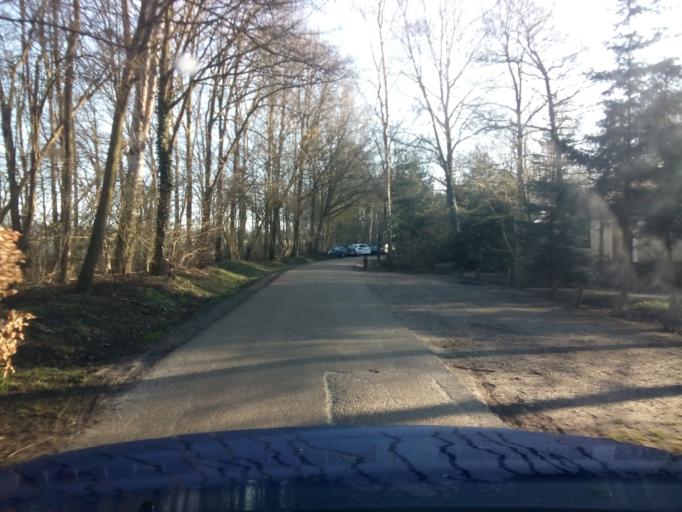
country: NL
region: Drenthe
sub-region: Gemeente Coevorden
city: Dalen
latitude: 52.6788
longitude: 6.7662
